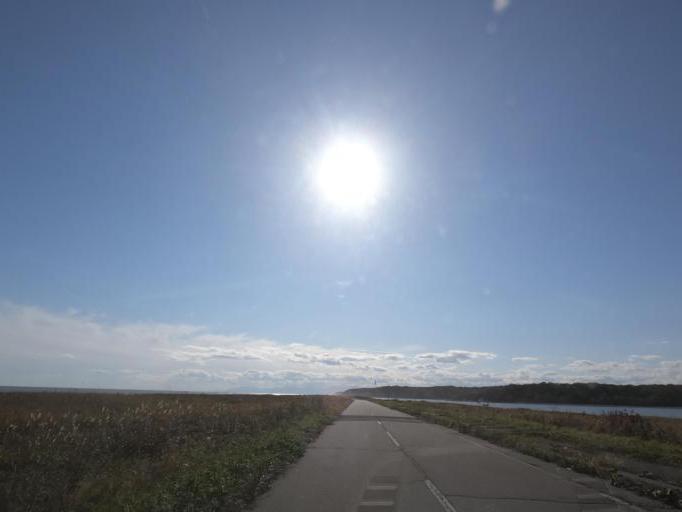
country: JP
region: Hokkaido
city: Obihiro
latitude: 42.5850
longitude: 143.5343
